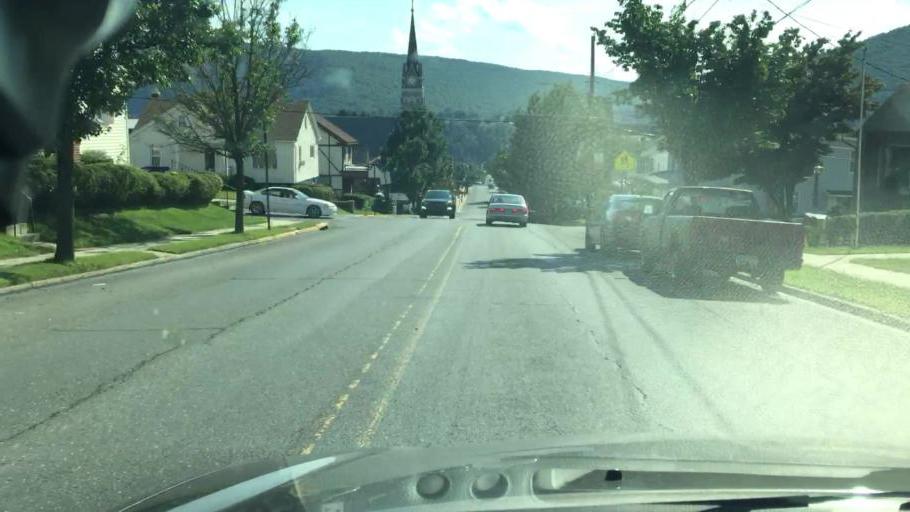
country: US
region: Pennsylvania
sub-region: Carbon County
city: Jim Thorpe
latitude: 40.8769
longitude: -75.7309
